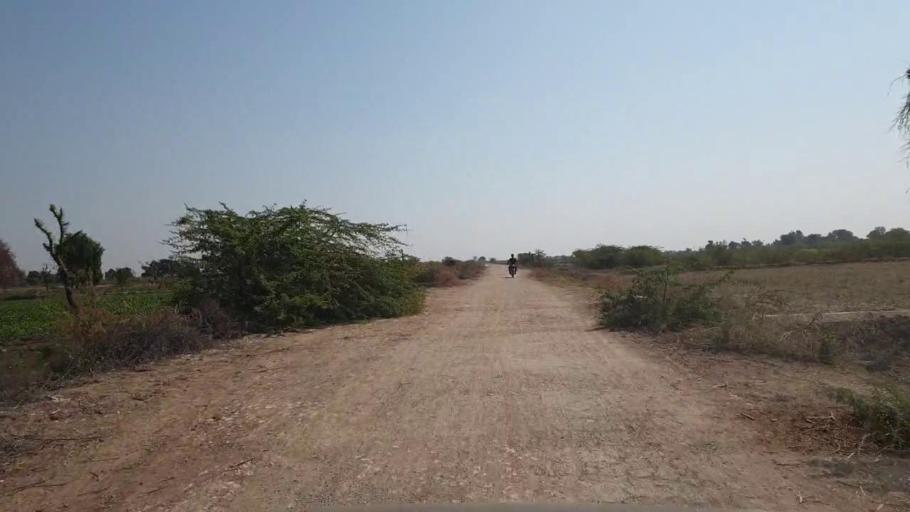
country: PK
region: Sindh
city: Samaro
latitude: 25.2503
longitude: 69.2796
